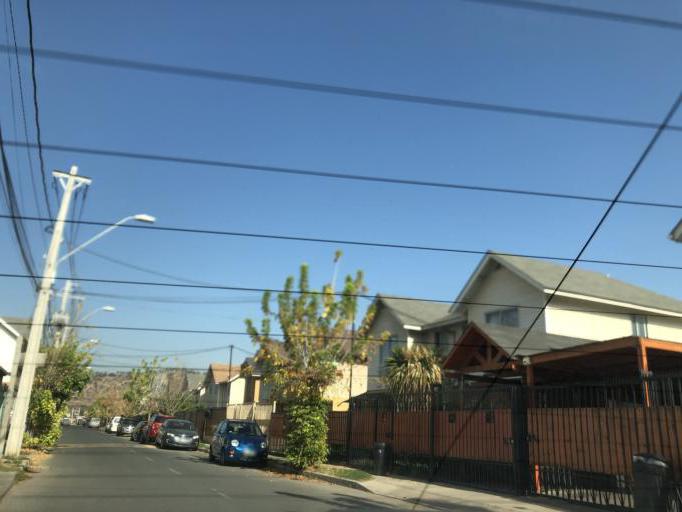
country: CL
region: Santiago Metropolitan
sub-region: Provincia de Cordillera
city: Puente Alto
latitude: -33.5968
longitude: -70.5480
